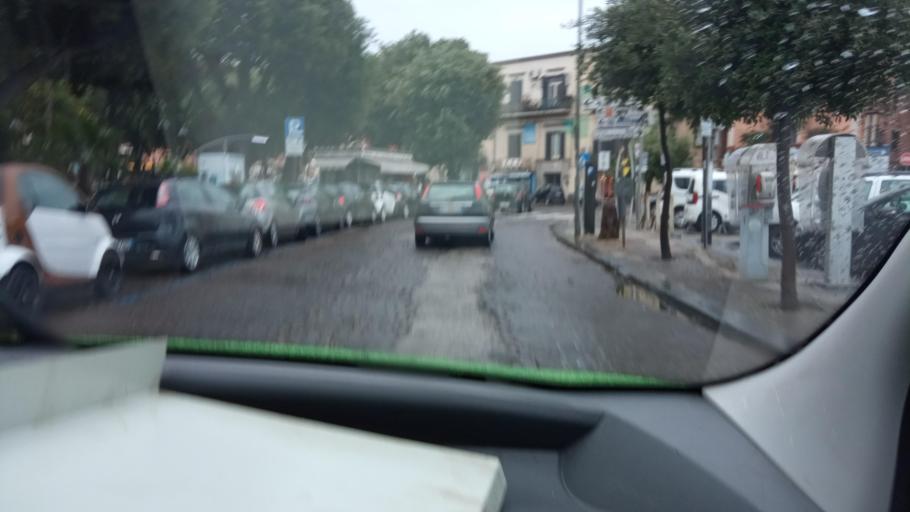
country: IT
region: Campania
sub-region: Provincia di Napoli
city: Pozzuoli
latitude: 40.8244
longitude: 14.1206
